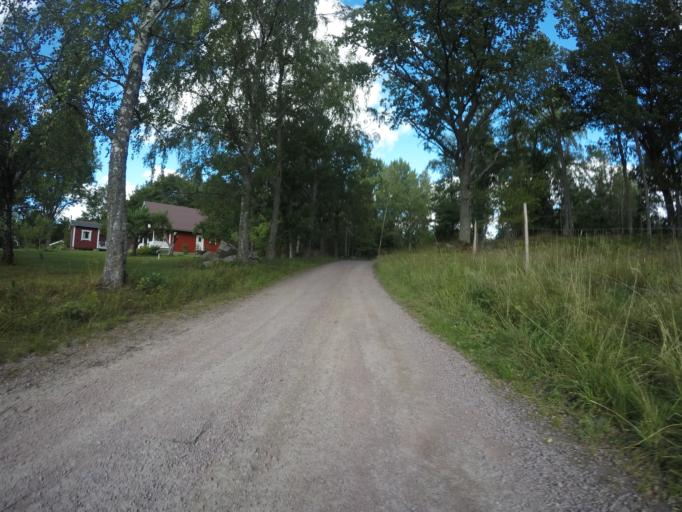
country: SE
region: Vaestmanland
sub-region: Hallstahammars Kommun
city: Kolback
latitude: 59.4914
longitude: 16.1939
